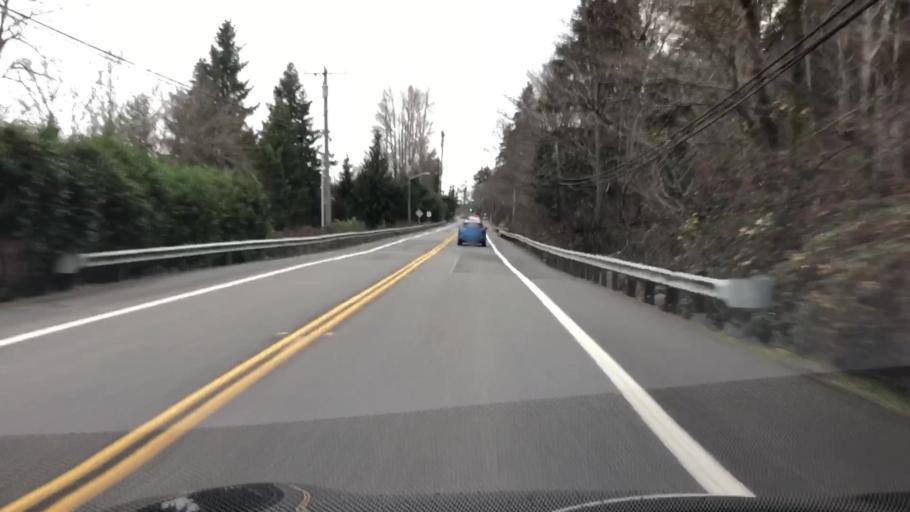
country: US
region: Washington
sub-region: King County
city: Sammamish
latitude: 47.6182
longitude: -122.0677
